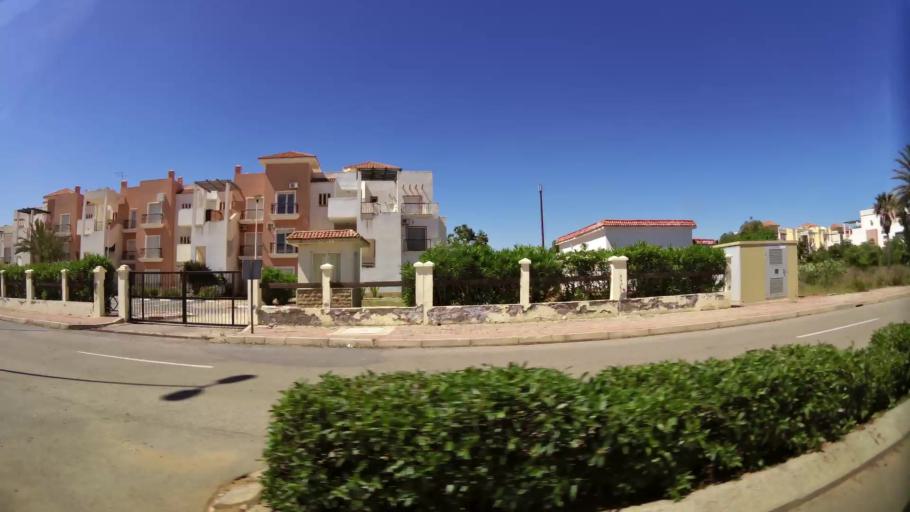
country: MA
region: Oriental
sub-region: Berkane-Taourirt
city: Madagh
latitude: 35.1011
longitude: -2.3021
